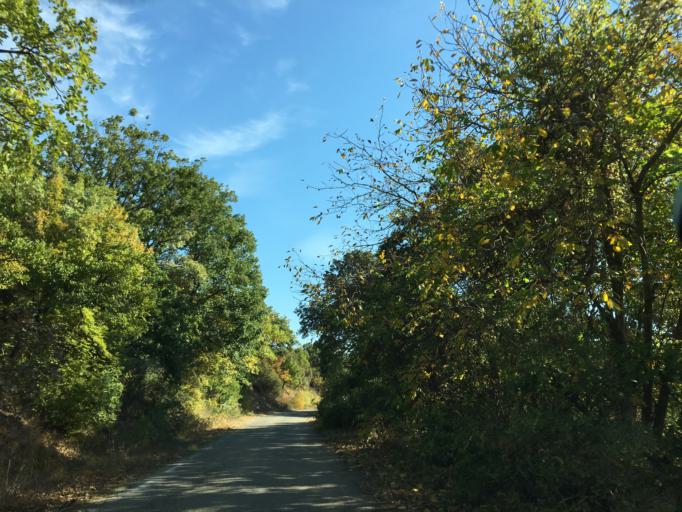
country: BG
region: Khaskovo
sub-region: Obshtina Ivaylovgrad
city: Ivaylovgrad
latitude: 41.4301
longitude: 26.1289
